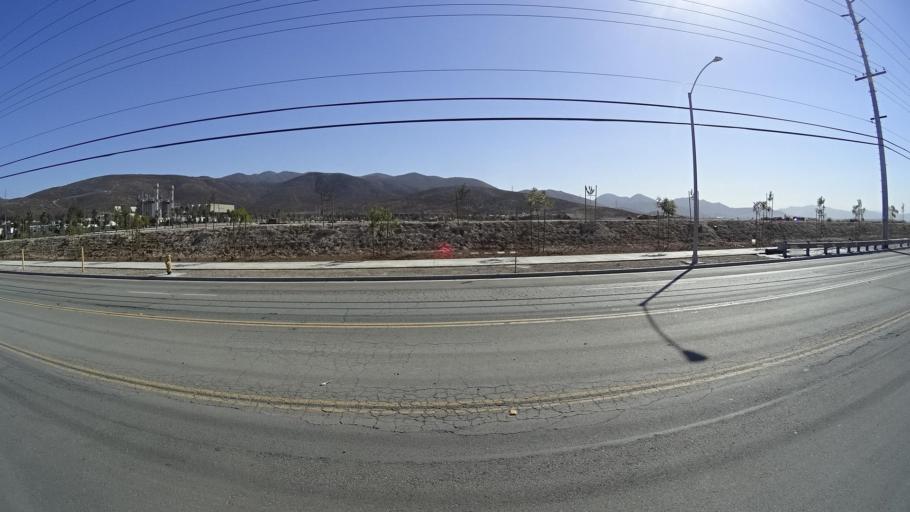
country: MX
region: Baja California
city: Tijuana
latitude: 32.5698
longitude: -116.9193
